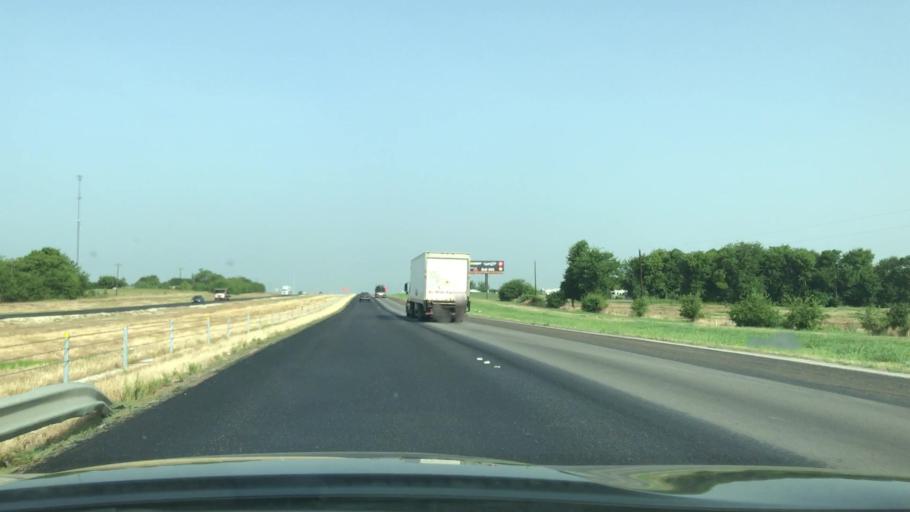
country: US
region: Texas
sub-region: Kaufman County
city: Terrell
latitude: 32.6826
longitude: -96.2006
